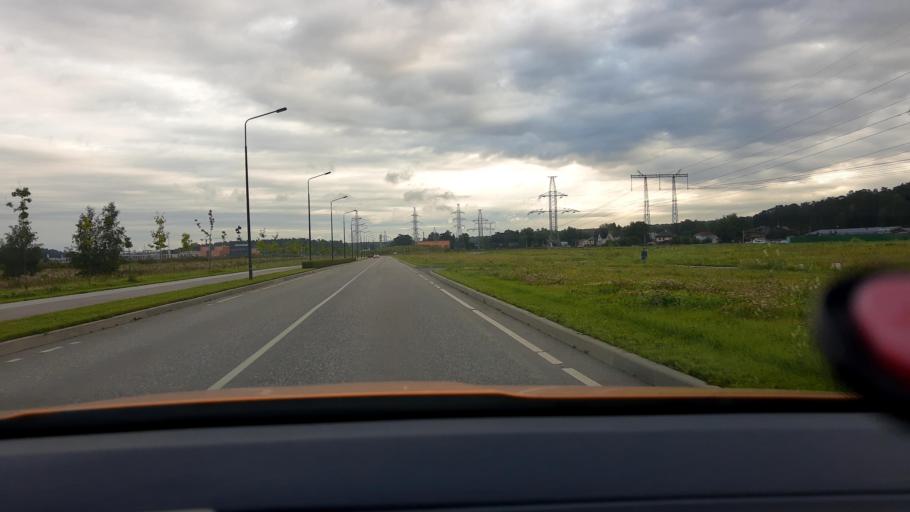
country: RU
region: Moskovskaya
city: Barvikha
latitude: 55.7502
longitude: 37.3118
